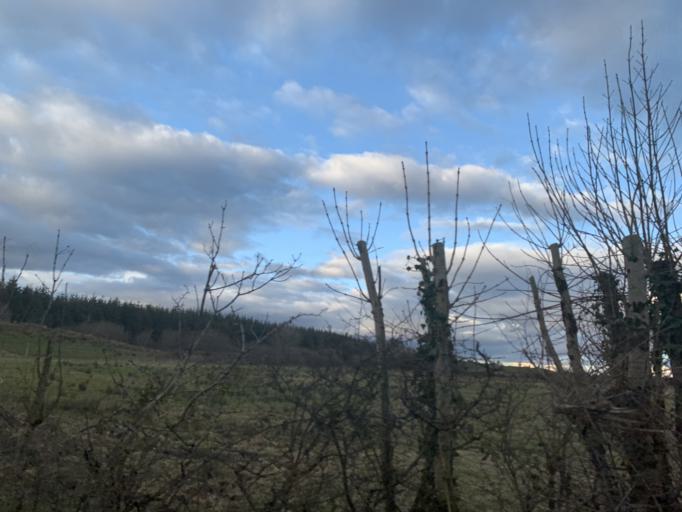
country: IE
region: Connaught
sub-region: Maigh Eo
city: Ballyhaunis
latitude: 53.8651
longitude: -8.7603
